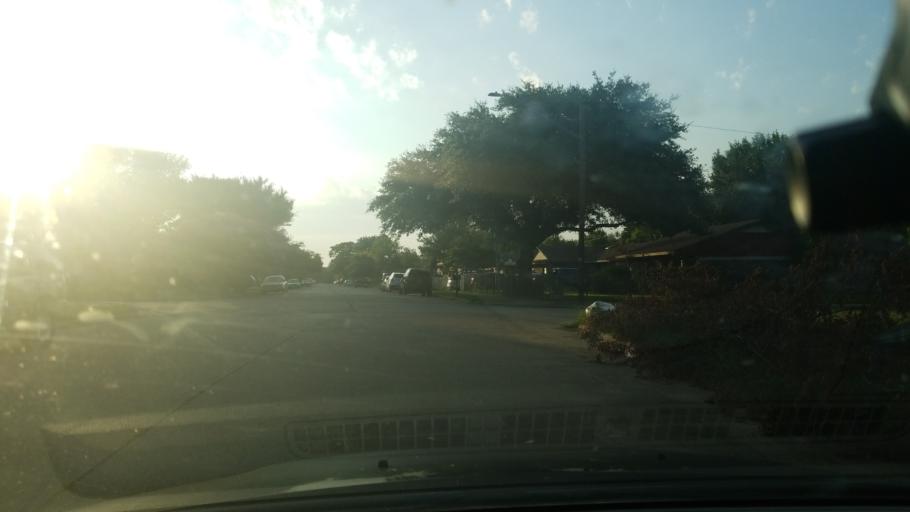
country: US
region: Texas
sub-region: Dallas County
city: Balch Springs
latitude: 32.7255
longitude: -96.6526
